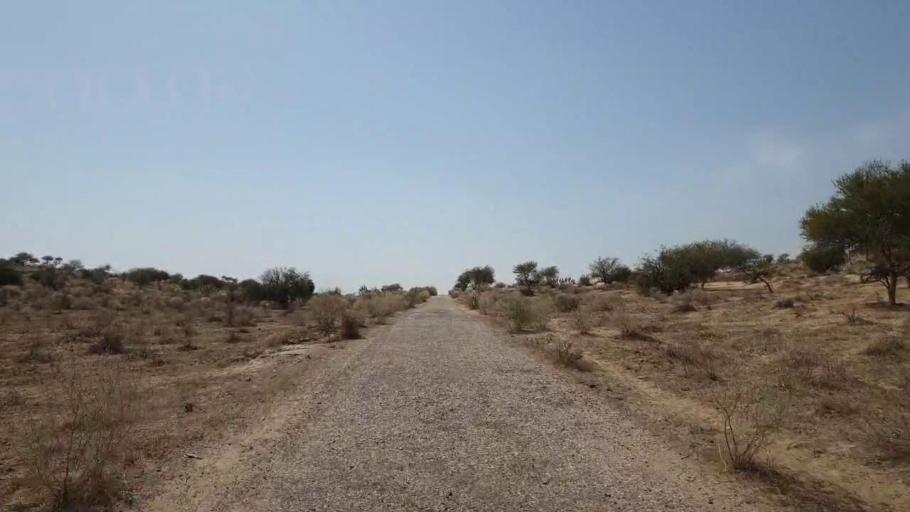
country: PK
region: Sindh
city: Umarkot
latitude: 25.2099
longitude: 69.9293
